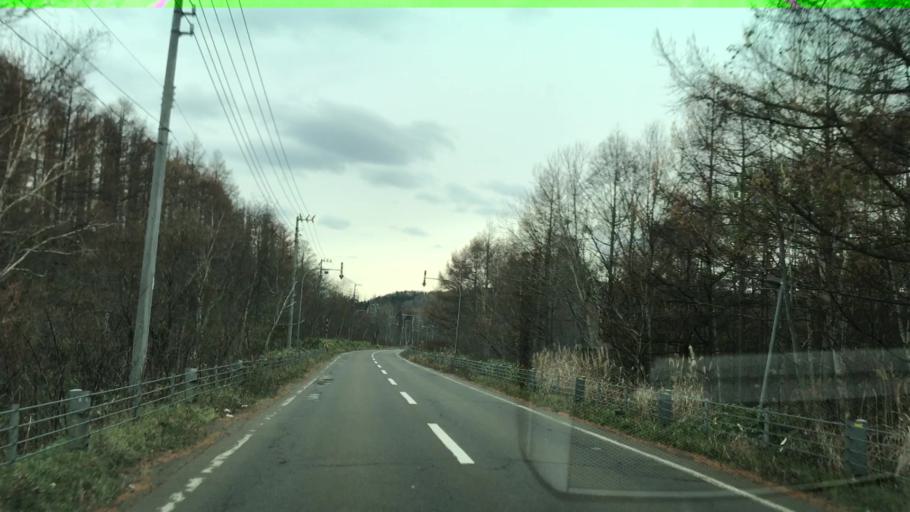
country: JP
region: Hokkaido
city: Yoichi
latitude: 43.3004
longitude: 140.5665
